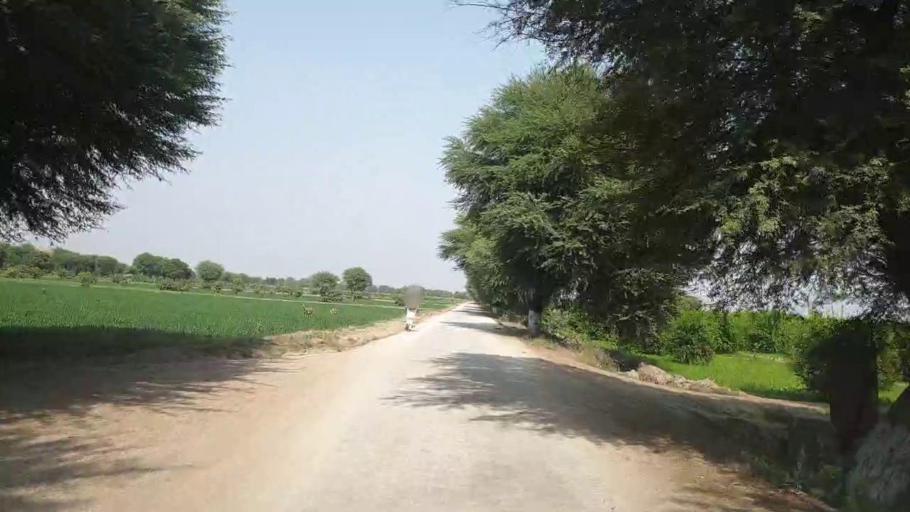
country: PK
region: Sindh
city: Dhoro Naro
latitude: 25.4855
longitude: 69.6244
